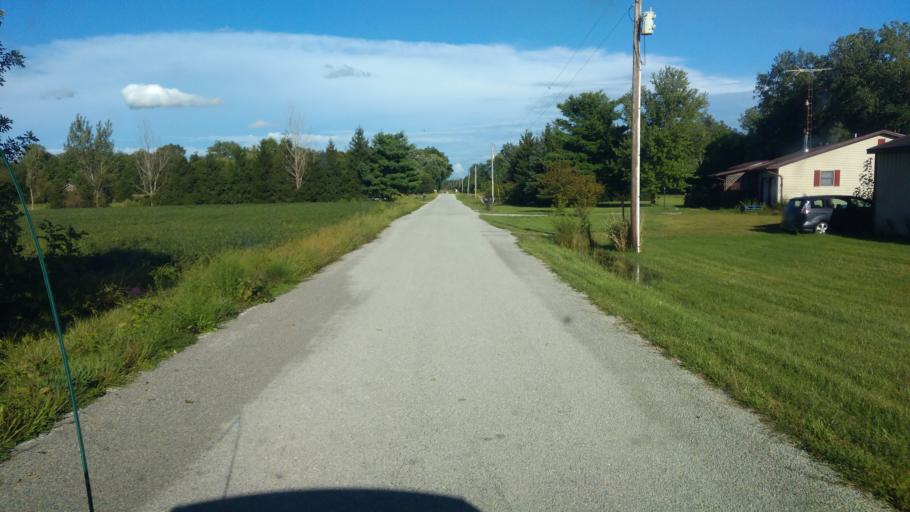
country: US
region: Ohio
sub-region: Hardin County
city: Forest
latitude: 40.7530
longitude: -83.5906
